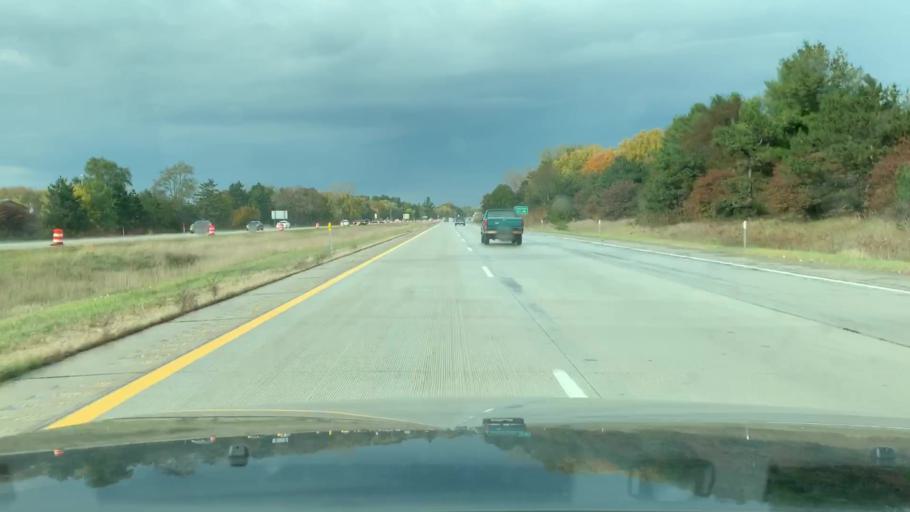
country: US
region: Michigan
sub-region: Ottawa County
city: Jenison
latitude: 42.8904
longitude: -85.7786
